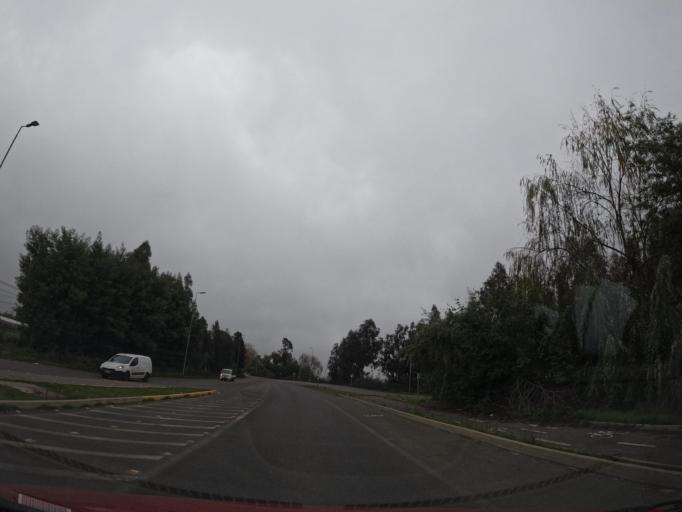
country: CL
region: Maule
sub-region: Provincia de Talca
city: San Clemente
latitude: -35.5504
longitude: -71.4712
